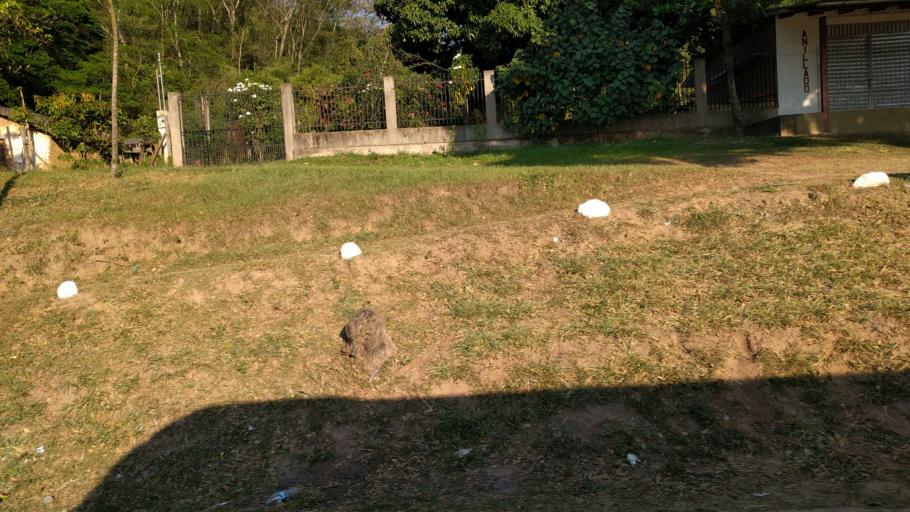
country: BO
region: Santa Cruz
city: Limoncito
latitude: -18.0238
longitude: -63.3999
